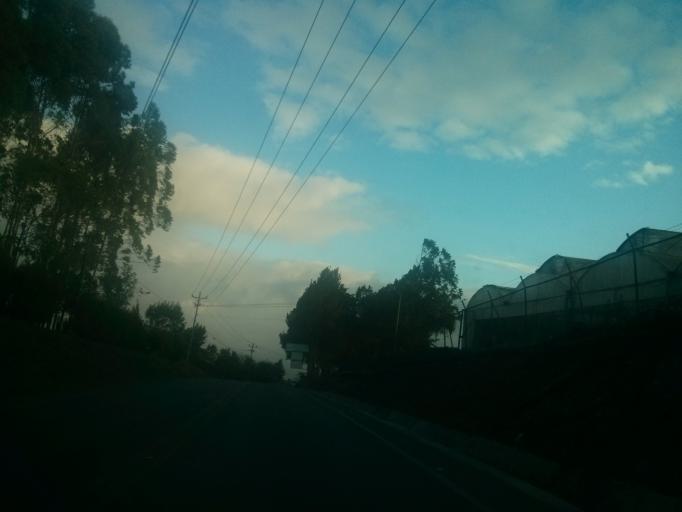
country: CR
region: Cartago
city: Cot
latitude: 9.8846
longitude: -83.8972
